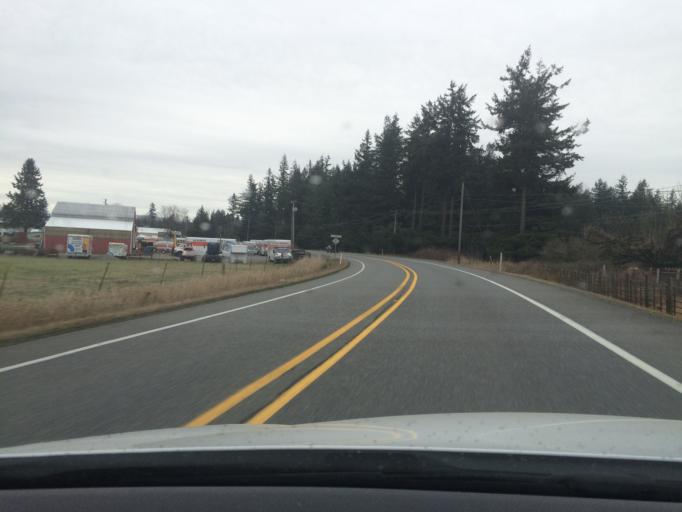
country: US
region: Washington
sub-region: Whatcom County
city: Everson
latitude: 48.9050
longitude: -122.3744
